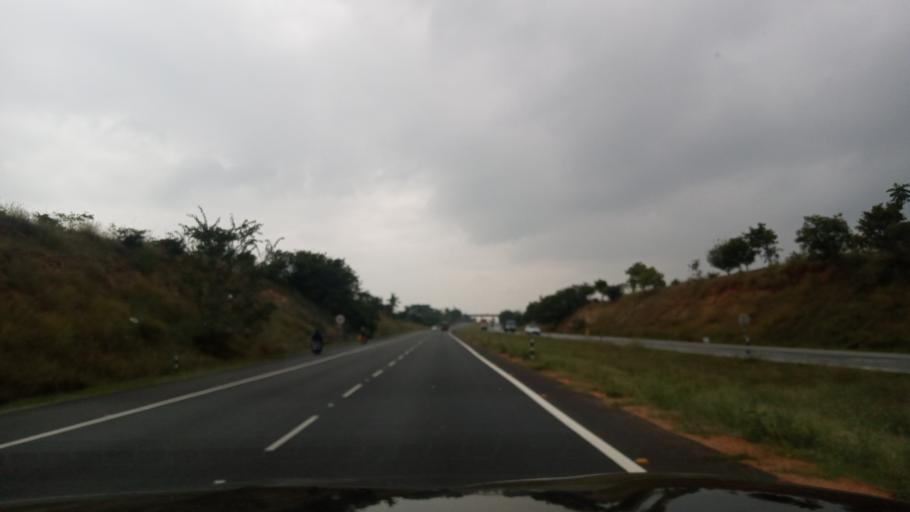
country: IN
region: Karnataka
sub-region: Bangalore Urban
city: Bangalore
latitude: 12.9777
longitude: 77.4712
